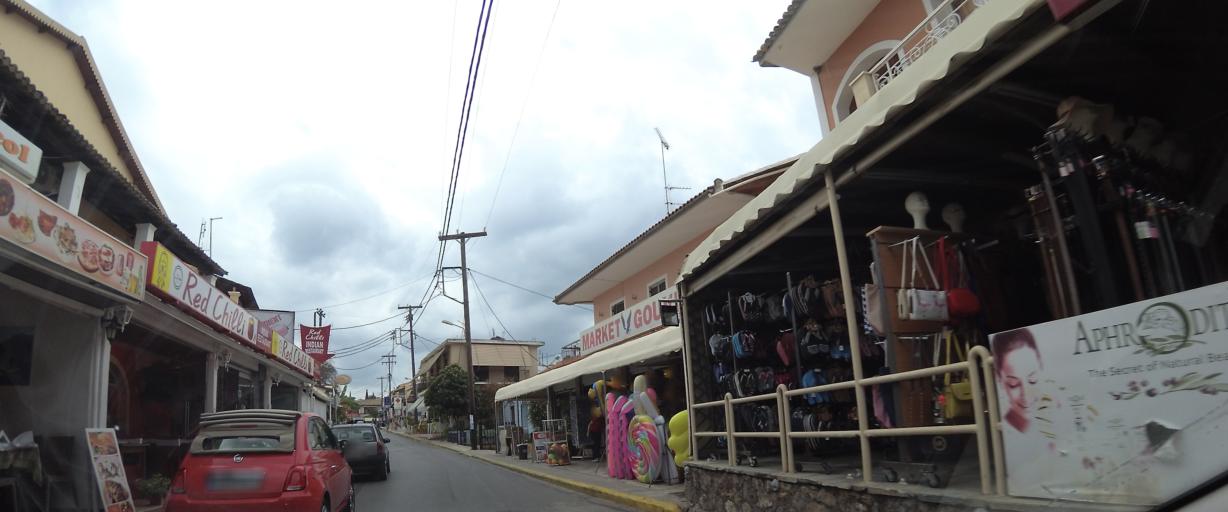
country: GR
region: Ionian Islands
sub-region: Nomos Kerkyras
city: Kontokali
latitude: 39.6526
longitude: 19.8441
